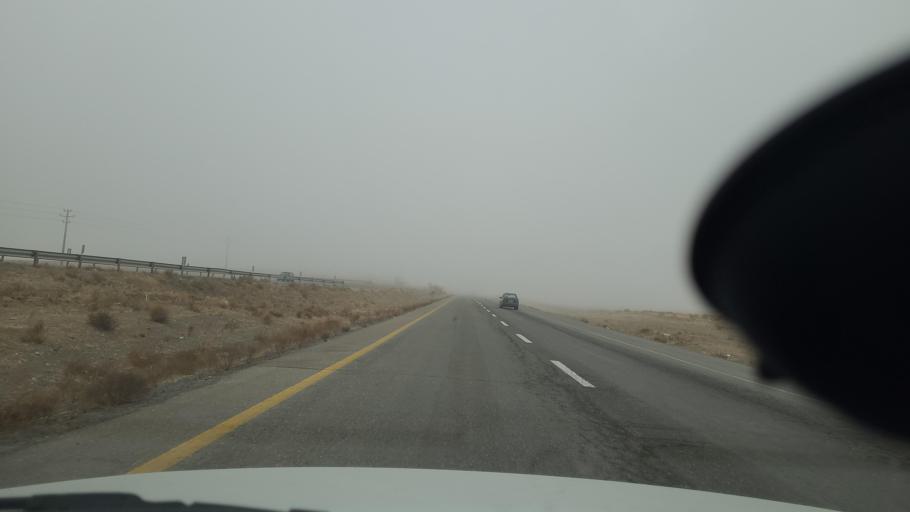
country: IR
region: Razavi Khorasan
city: Fariman
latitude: 35.8076
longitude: 59.7456
